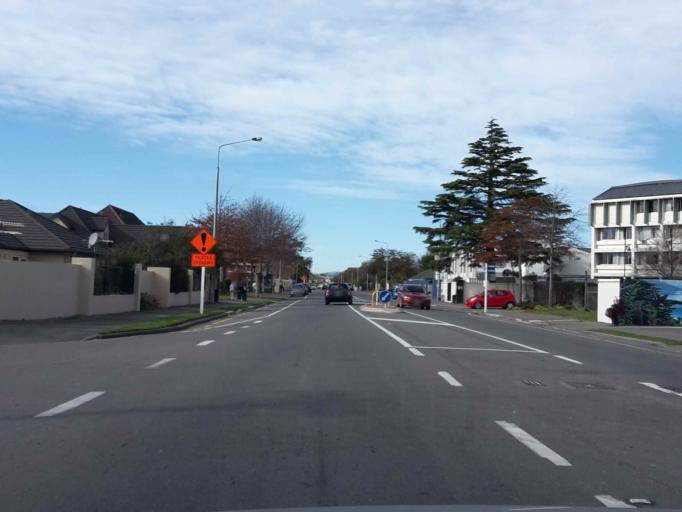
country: NZ
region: Canterbury
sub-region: Christchurch City
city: Christchurch
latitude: -43.4937
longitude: 172.6014
